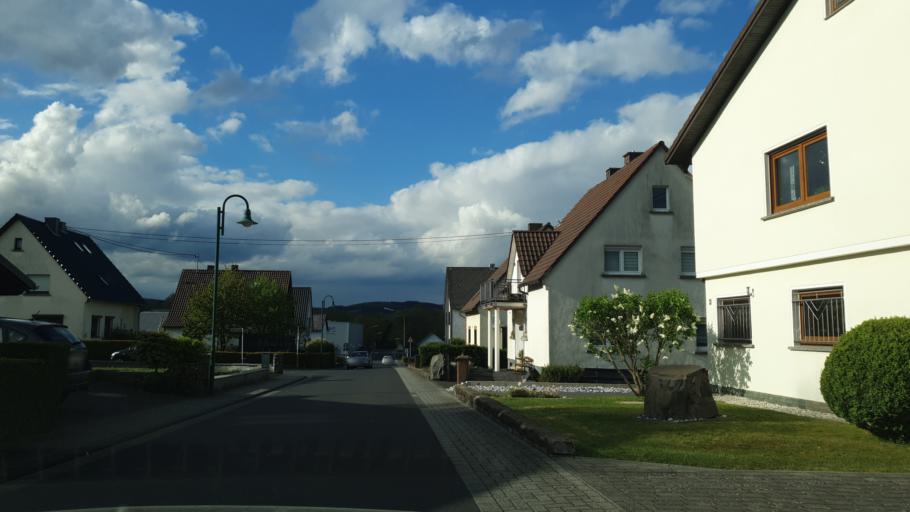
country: DE
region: Rheinland-Pfalz
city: Enspel
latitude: 50.6299
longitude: 7.8968
